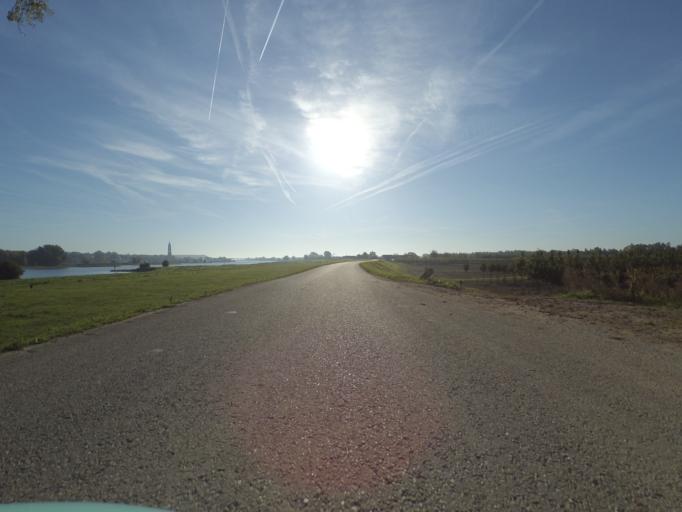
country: NL
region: Utrecht
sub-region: Gemeente Rhenen
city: Rhenen
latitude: 51.9587
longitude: 5.5457
